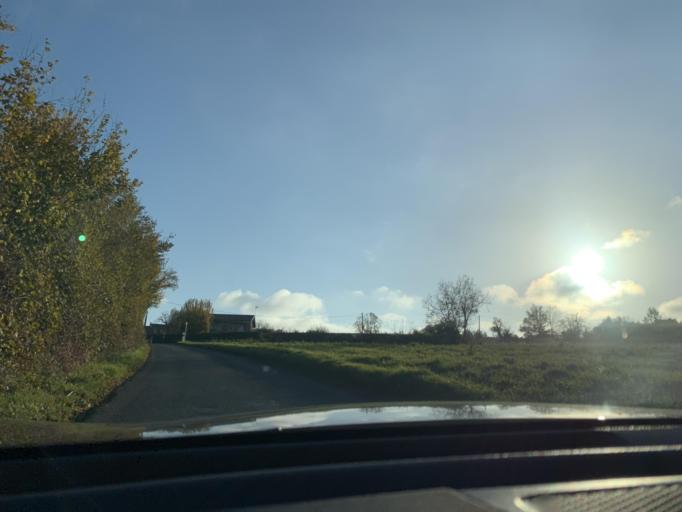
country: FR
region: Rhone-Alpes
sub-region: Departement du Rhone
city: Pommiers
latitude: 45.9432
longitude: 4.6812
